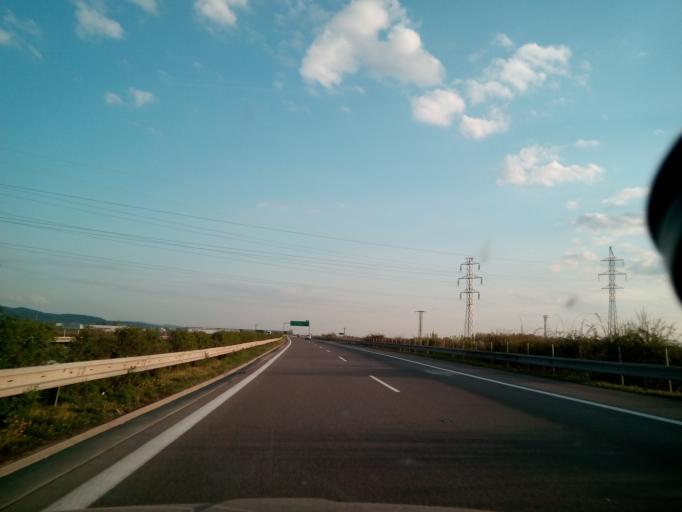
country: SK
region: Trenciansky
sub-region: Okres Nove Mesto nad Vahom
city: Nove Mesto nad Vahom
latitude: 48.7765
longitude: 17.8775
